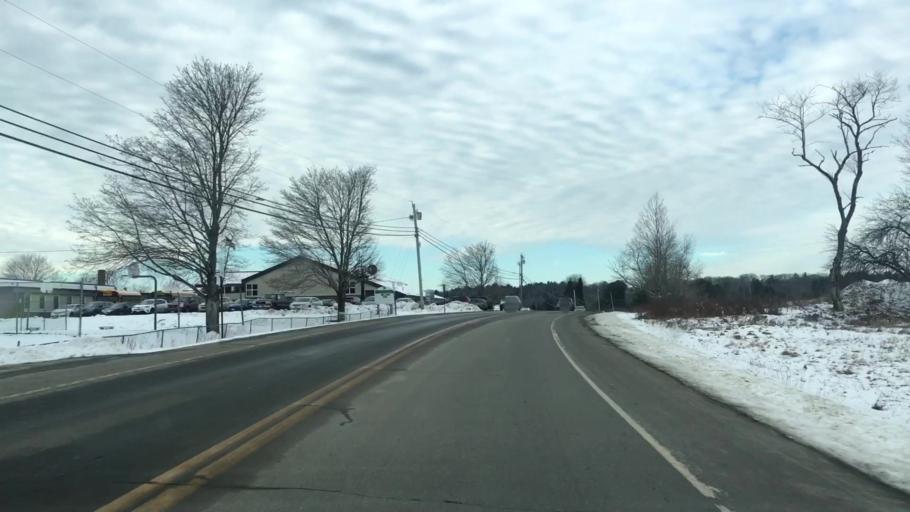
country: US
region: Maine
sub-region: Lincoln County
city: Whitefield
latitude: 44.2230
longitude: -69.6020
